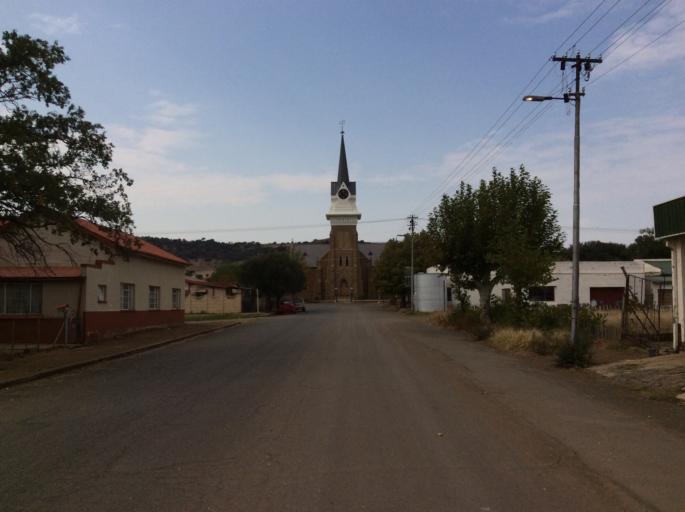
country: LS
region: Mafeteng
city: Mafeteng
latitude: -29.7276
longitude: 27.0427
